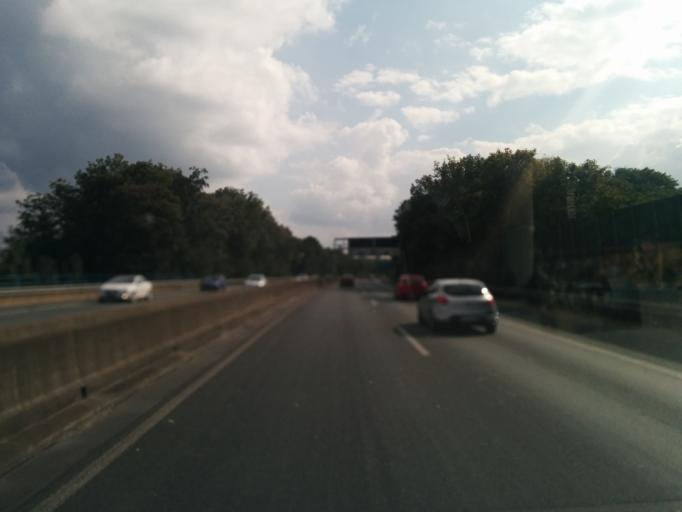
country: DE
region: North Rhine-Westphalia
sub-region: Regierungsbezirk Munster
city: Recklinghausen
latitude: 51.6006
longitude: 7.1842
